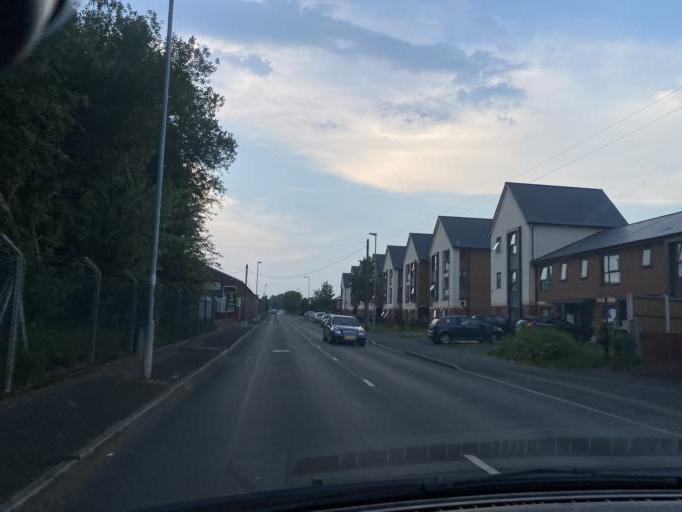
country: GB
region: England
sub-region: Borough of Tameside
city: Denton
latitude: 53.4642
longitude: -2.1230
